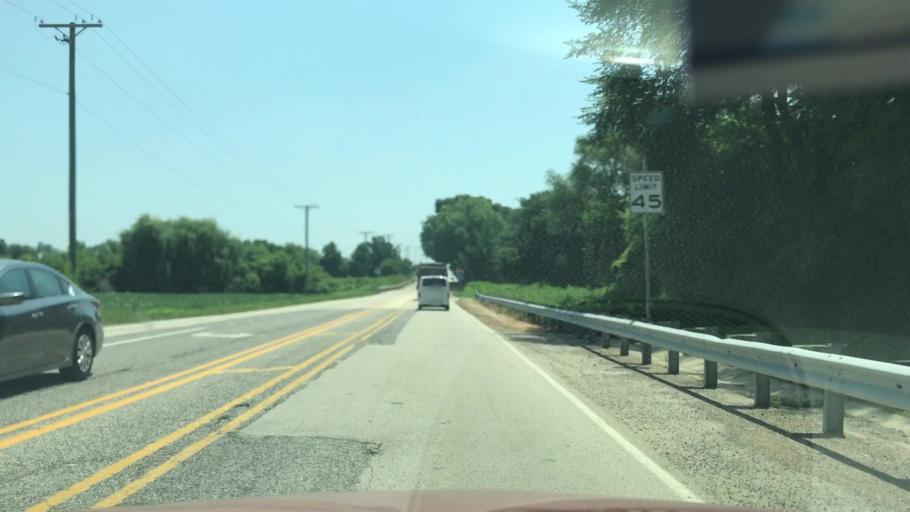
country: US
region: Illinois
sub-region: Winnebago County
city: Cherry Valley
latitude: 42.2392
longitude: -88.9007
